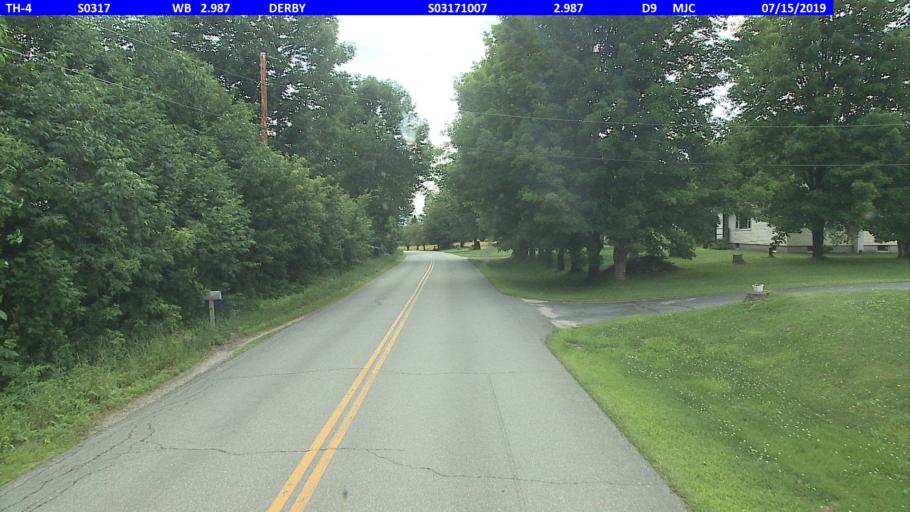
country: US
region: Vermont
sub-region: Orleans County
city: Newport
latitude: 44.9874
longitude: -72.1651
